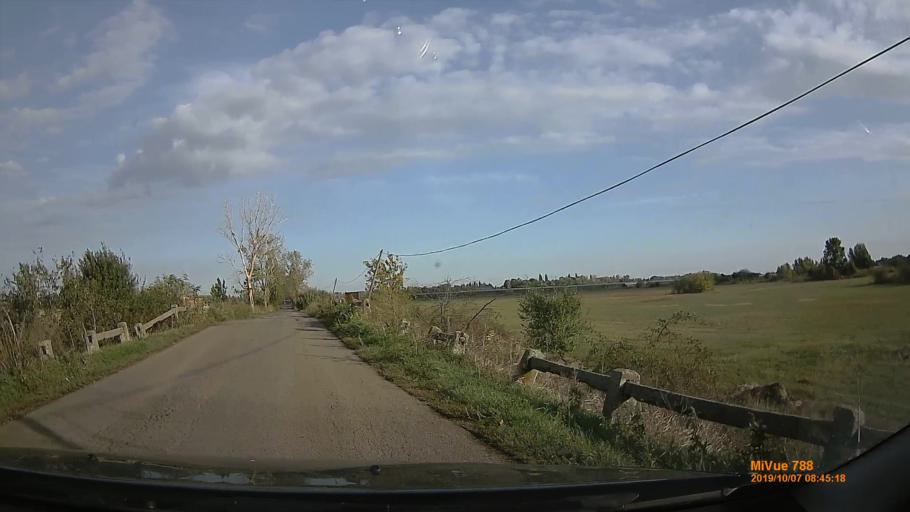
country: HU
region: Bekes
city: Szarvas
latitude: 46.8130
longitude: 20.5267
